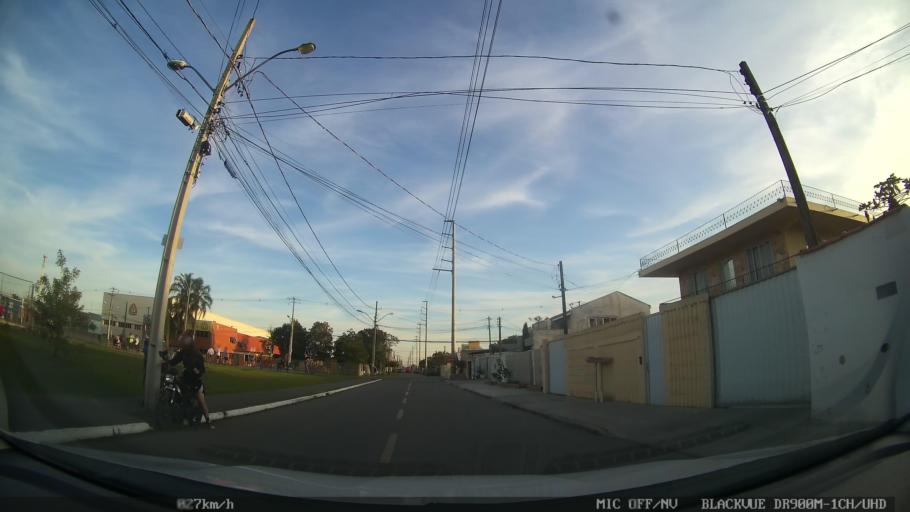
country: BR
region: Parana
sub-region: Pinhais
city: Pinhais
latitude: -25.4447
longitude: -49.1682
